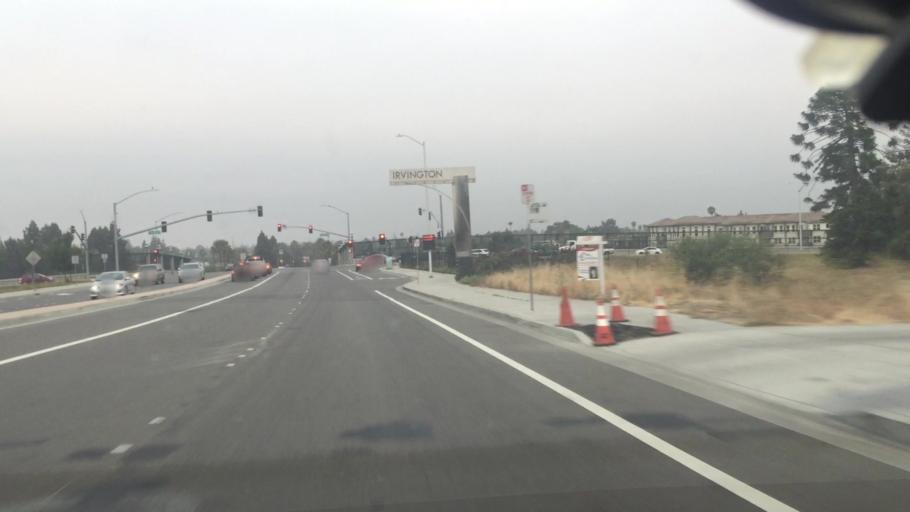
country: US
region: California
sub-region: Alameda County
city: Fremont
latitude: 37.5336
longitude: -121.9519
